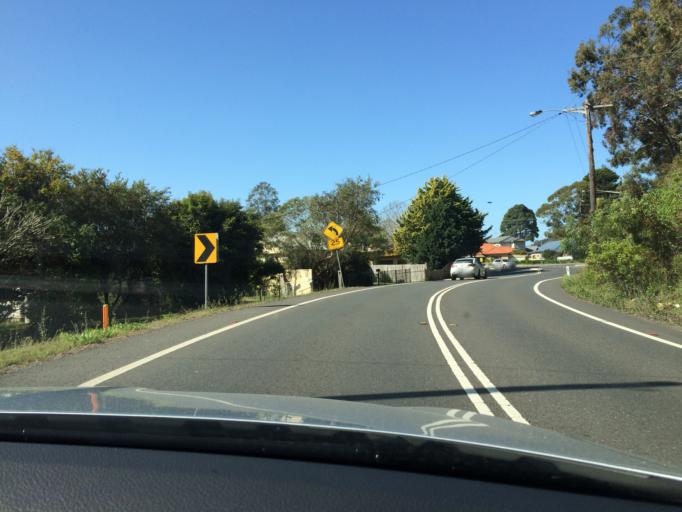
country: AU
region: New South Wales
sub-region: Gosford Shire
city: Blackwall
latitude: -33.5029
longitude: 151.3305
